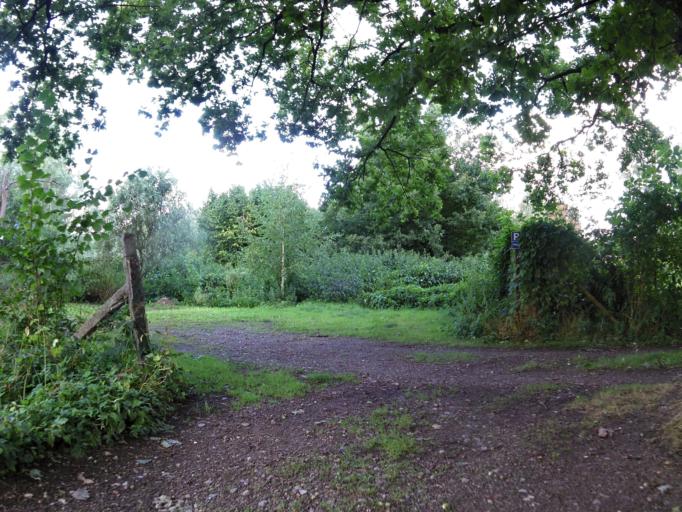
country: DE
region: Brandenburg
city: Storkow
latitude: 52.2588
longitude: 13.9295
